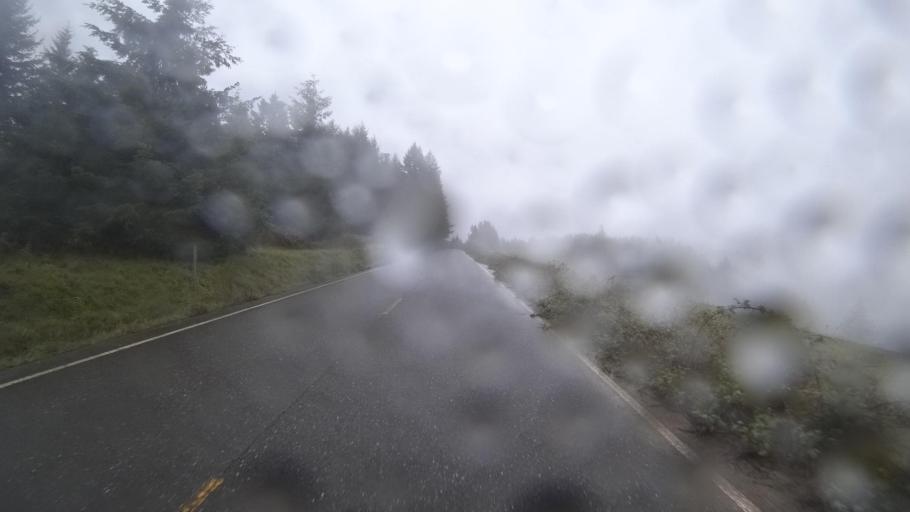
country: US
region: California
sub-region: Humboldt County
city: Westhaven-Moonstone
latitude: 41.1867
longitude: -123.9282
